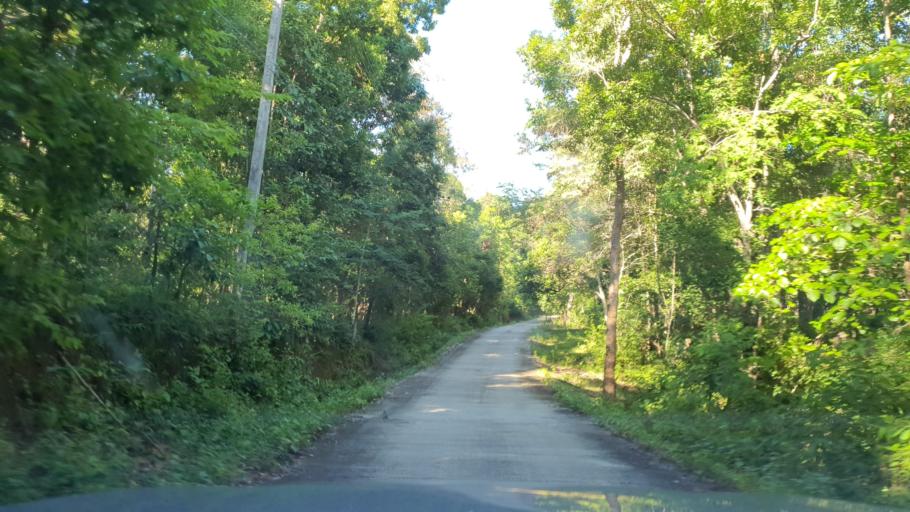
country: TH
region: Chiang Mai
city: Mae On
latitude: 18.8086
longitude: 99.3106
